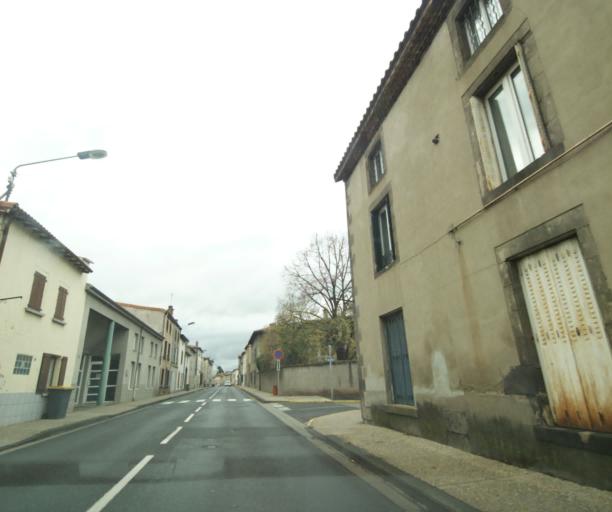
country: FR
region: Auvergne
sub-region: Departement du Puy-de-Dome
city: Pont-du-Chateau
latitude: 45.7994
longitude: 3.2468
